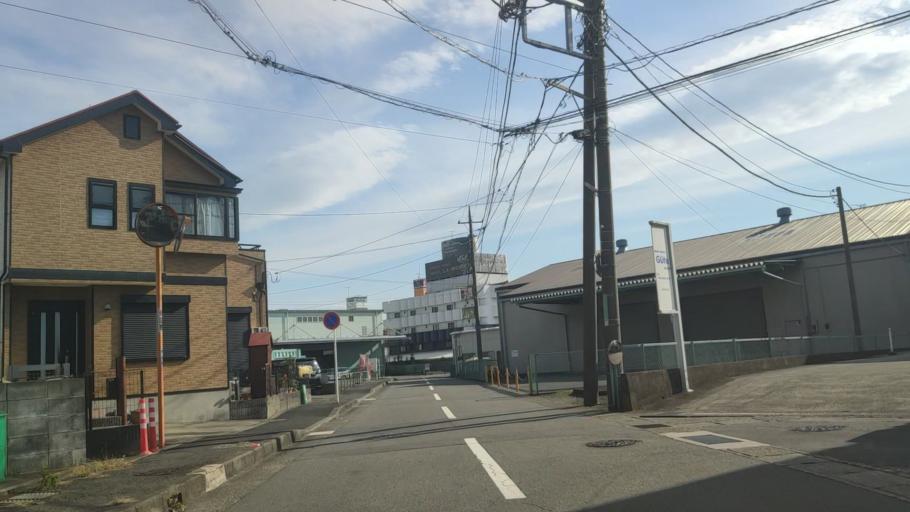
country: JP
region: Kanagawa
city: Atsugi
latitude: 35.4280
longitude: 139.3611
